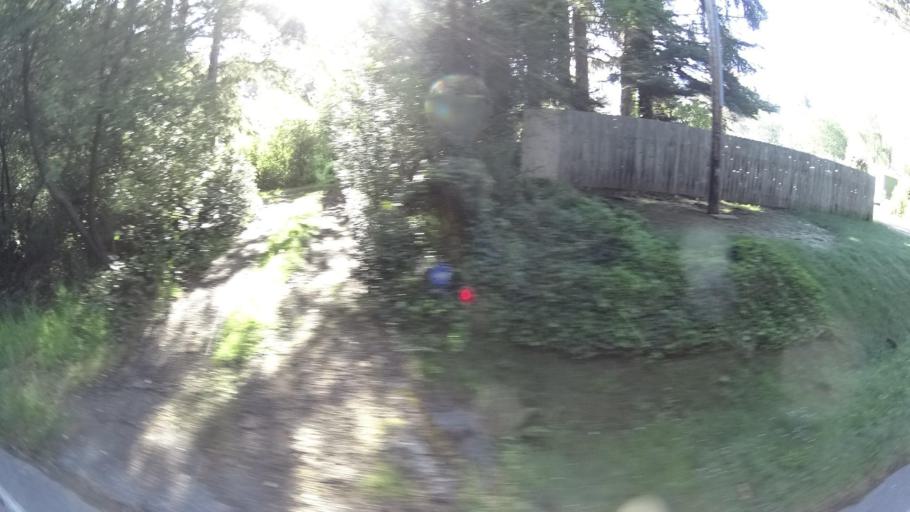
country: US
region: California
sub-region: Humboldt County
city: Westhaven-Moonstone
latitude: 41.1265
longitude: -124.1558
